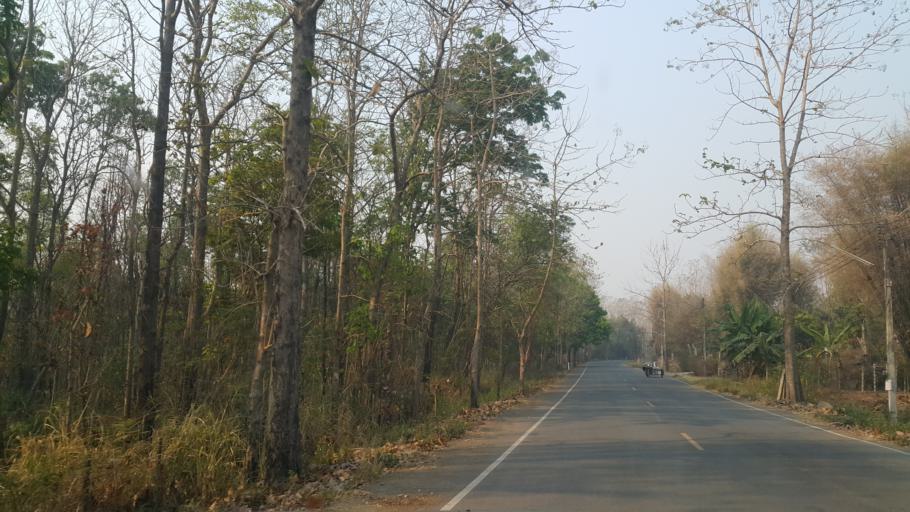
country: TH
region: Chiang Mai
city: Mae On
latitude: 18.7838
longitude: 99.2492
